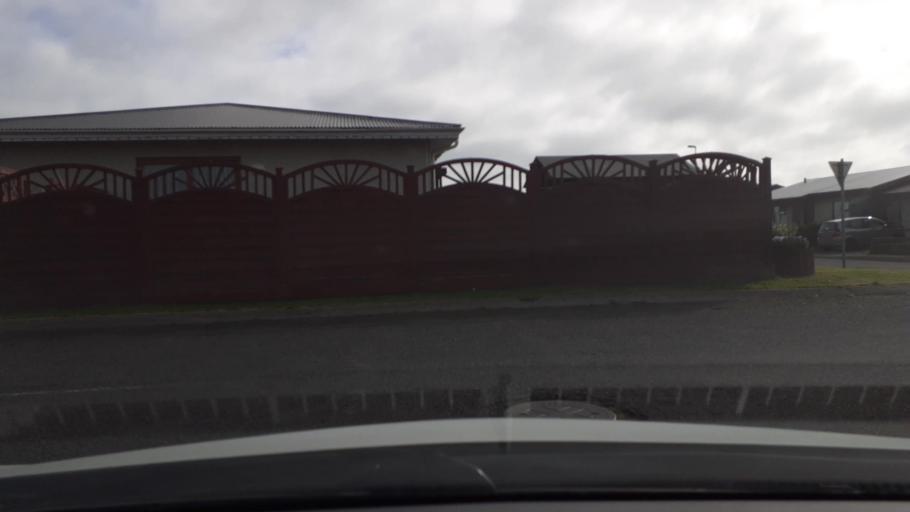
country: IS
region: South
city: THorlakshoefn
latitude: 63.8584
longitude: -21.3911
